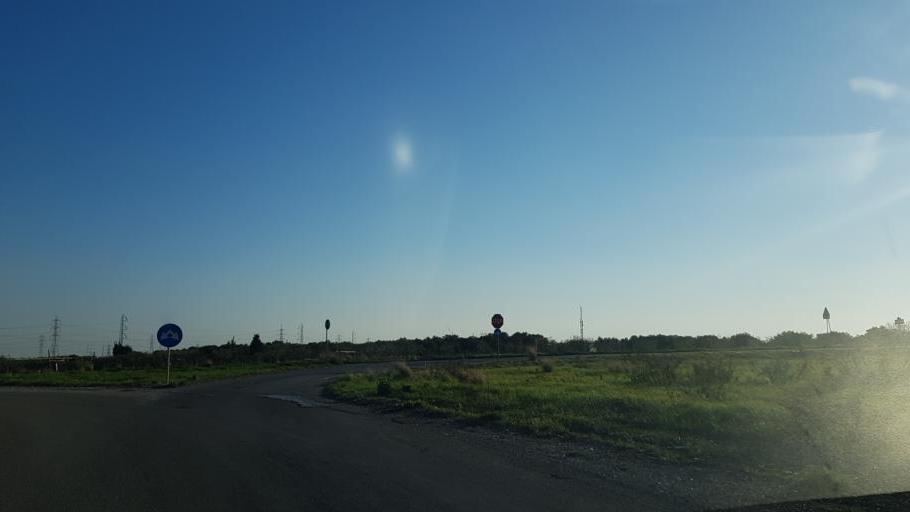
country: IT
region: Apulia
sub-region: Provincia di Brindisi
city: La Rosa
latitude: 40.6172
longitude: 17.9698
